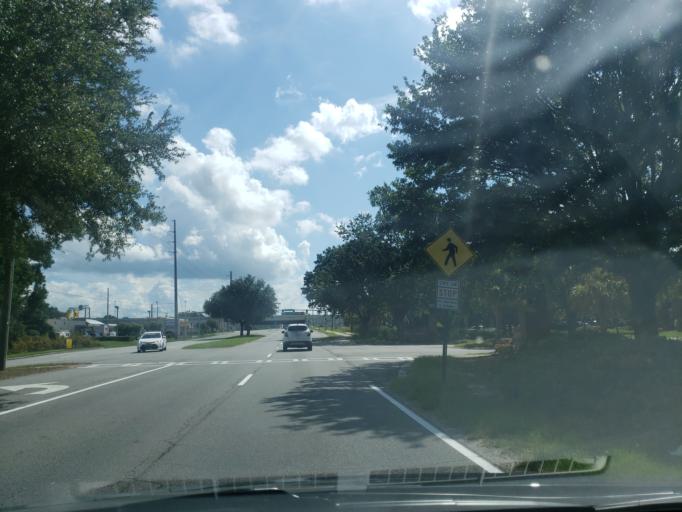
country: US
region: Georgia
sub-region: Chatham County
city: Georgetown
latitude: 31.9842
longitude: -81.2207
